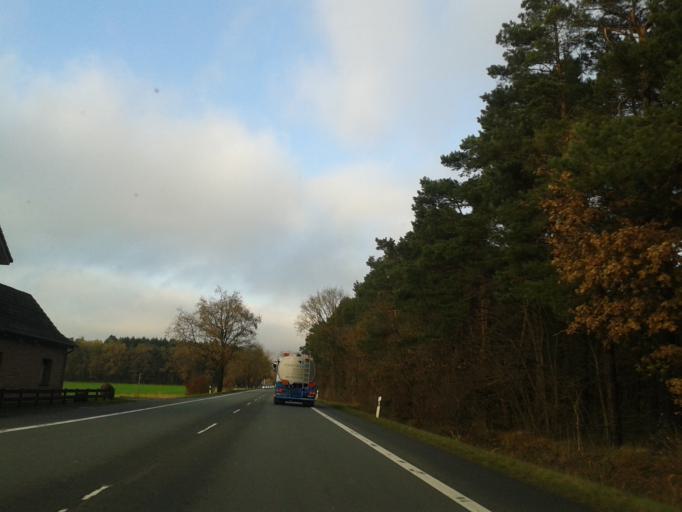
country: DE
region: North Rhine-Westphalia
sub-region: Regierungsbezirk Detmold
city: Augustdorf
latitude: 51.8878
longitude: 8.6746
